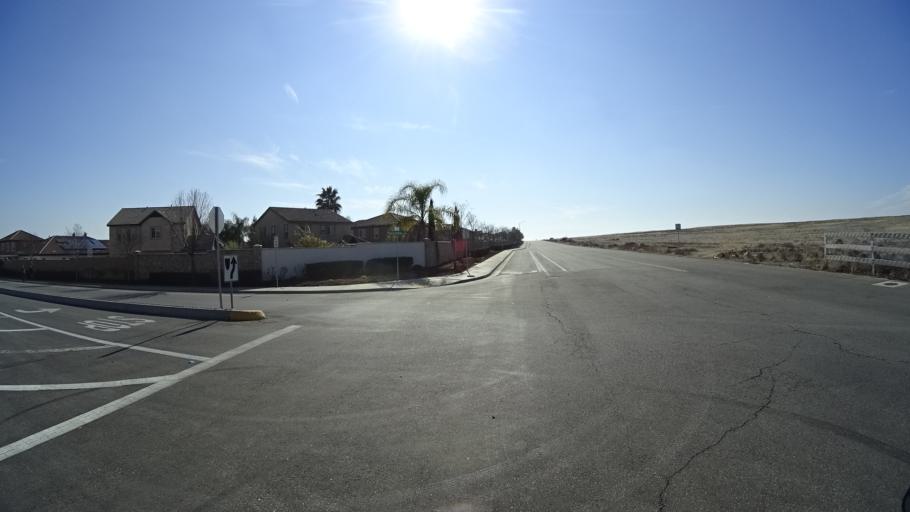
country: US
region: California
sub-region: Kern County
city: Oildale
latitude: 35.4068
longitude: -118.8962
